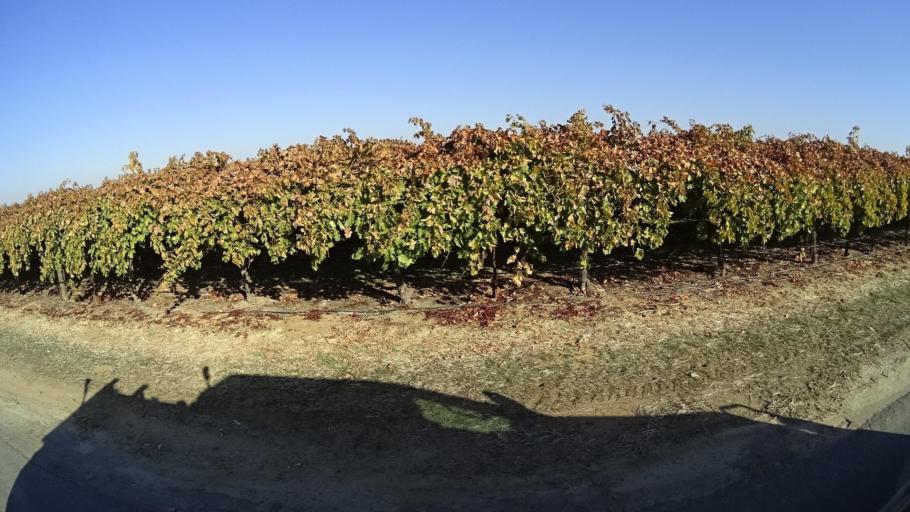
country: US
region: California
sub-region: Kern County
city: McFarland
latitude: 35.7253
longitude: -119.1633
